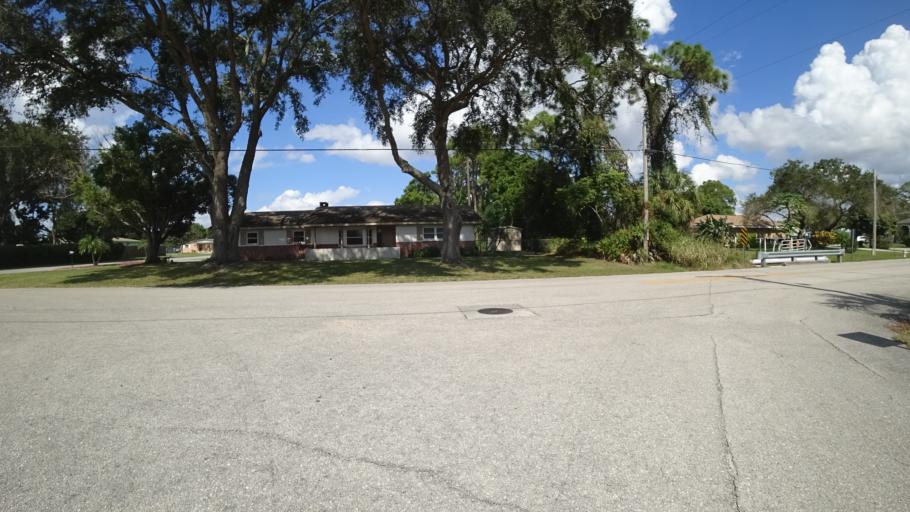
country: US
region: Florida
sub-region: Manatee County
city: Whitfield
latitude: 27.4224
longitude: -82.5633
